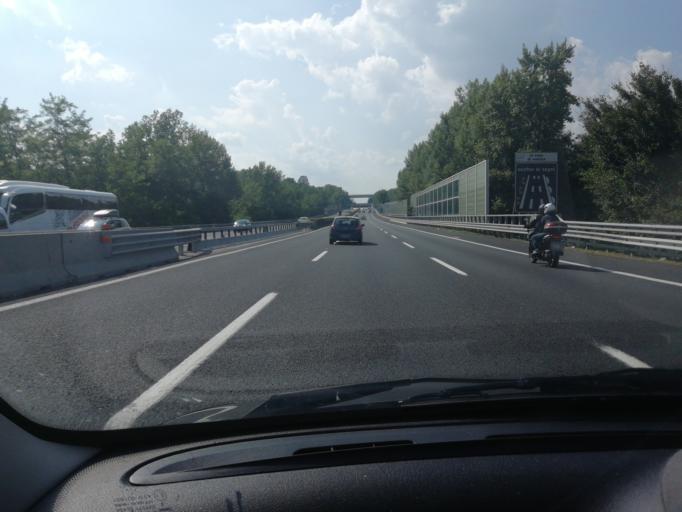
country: IT
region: Latium
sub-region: Provincia di Frosinone
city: Arnara
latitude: 41.5672
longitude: 13.3906
